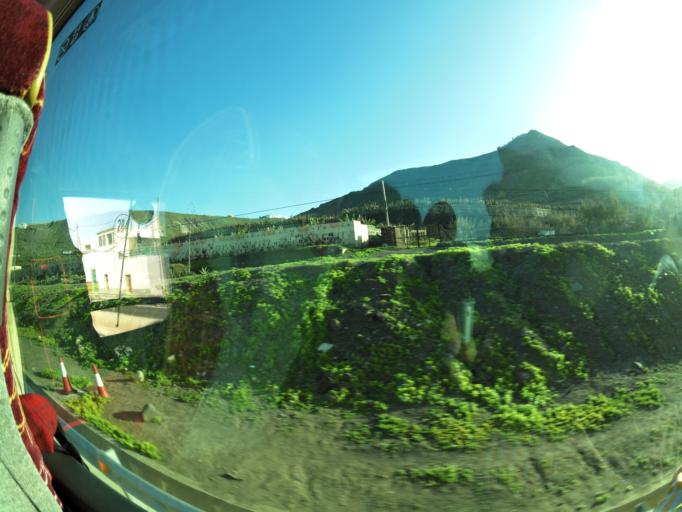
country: ES
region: Canary Islands
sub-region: Provincia de Las Palmas
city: Arucas
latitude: 28.1459
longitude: -15.5468
